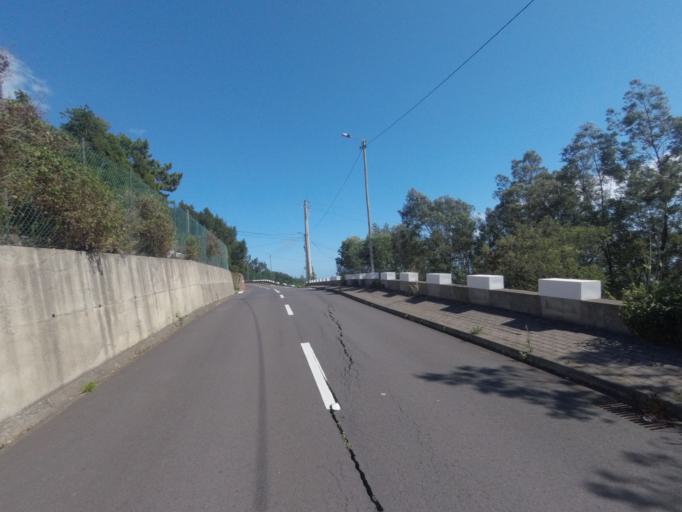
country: PT
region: Madeira
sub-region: Ribeira Brava
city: Campanario
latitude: 32.6819
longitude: -17.0411
